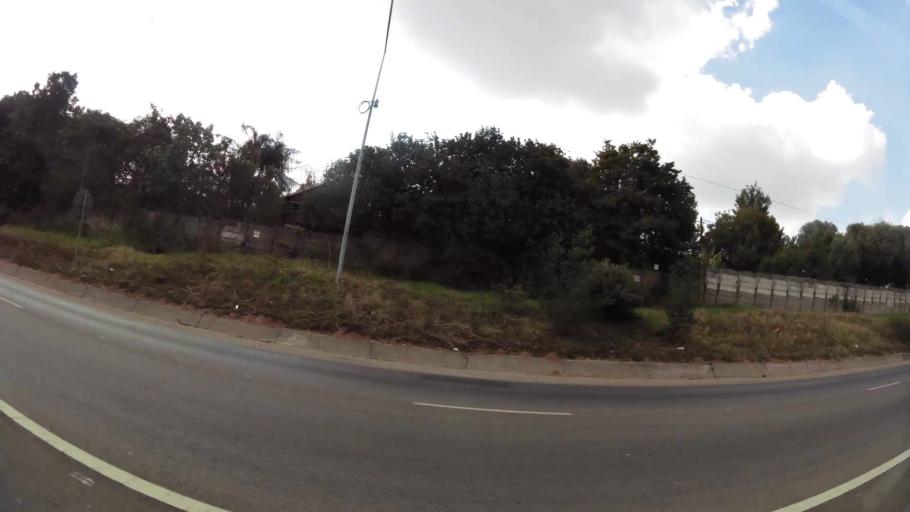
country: ZA
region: Gauteng
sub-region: City of Tshwane Metropolitan Municipality
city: Centurion
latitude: -25.8188
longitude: 28.2501
